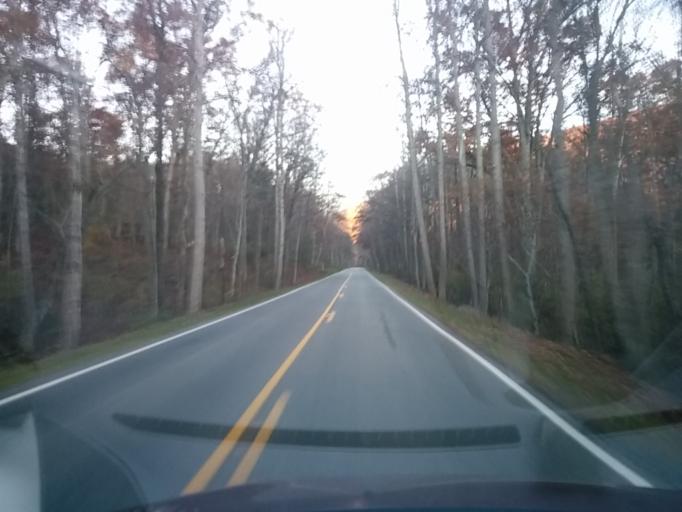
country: US
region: Virginia
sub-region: Rockbridge County
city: East Lexington
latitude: 37.9611
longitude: -79.4796
